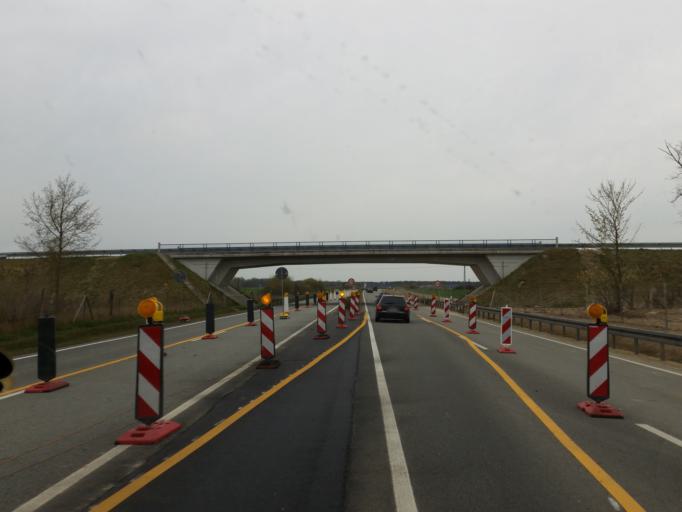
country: DE
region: Mecklenburg-Vorpommern
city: Grimmen
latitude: 54.1006
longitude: 13.1406
